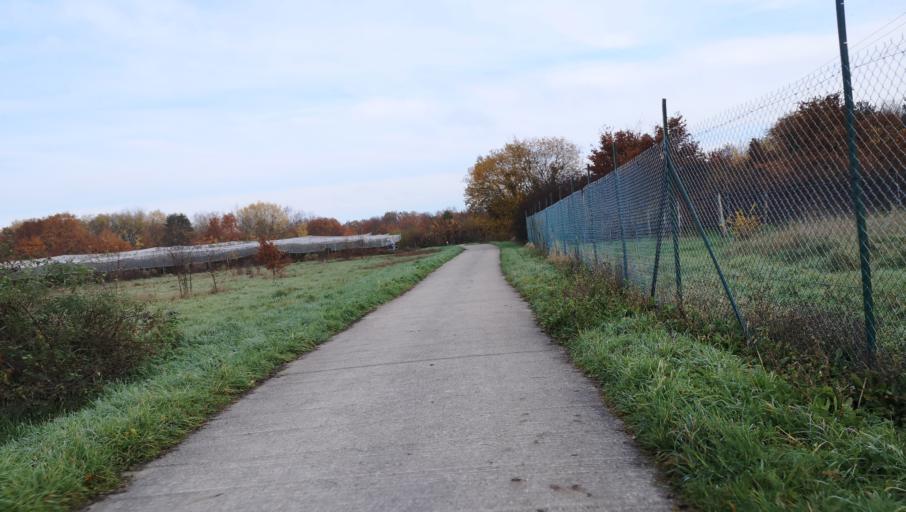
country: FR
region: Centre
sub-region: Departement du Loiret
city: Semoy
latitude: 47.9381
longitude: 1.9556
